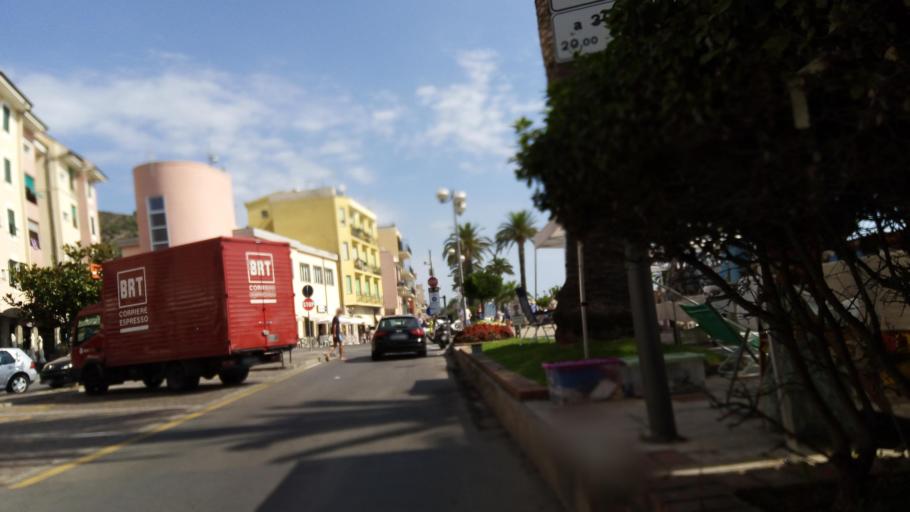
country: IT
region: Liguria
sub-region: Provincia di Savona
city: Ceriale
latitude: 44.0947
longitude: 8.2325
